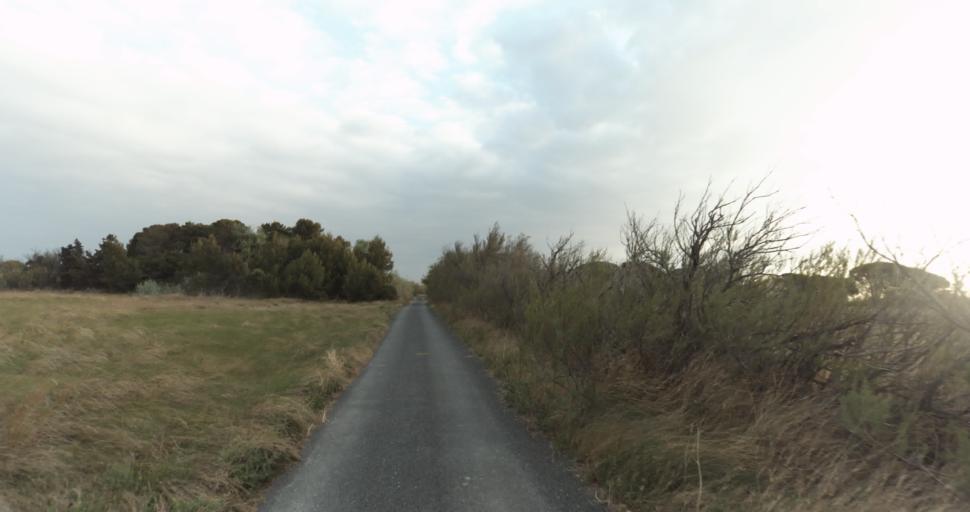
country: FR
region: Languedoc-Roussillon
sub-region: Departement de l'Aude
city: Leucate
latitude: 42.9470
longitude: 3.0296
